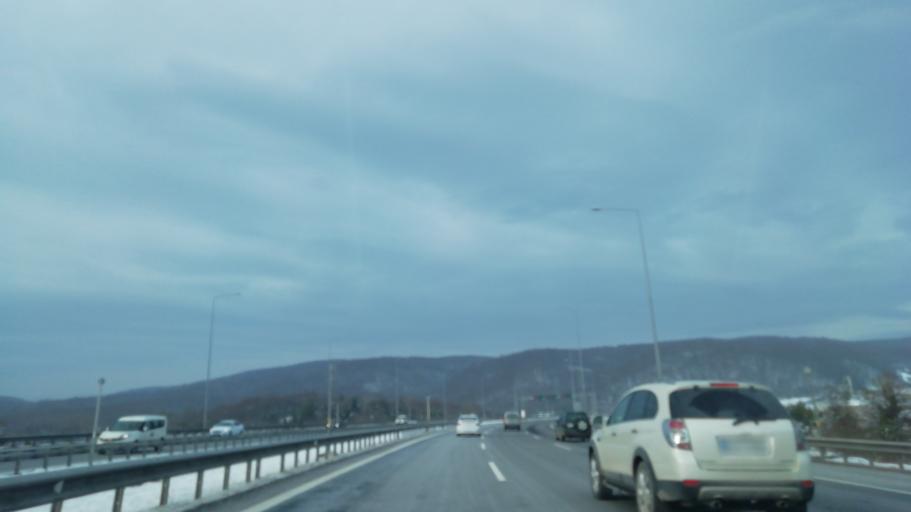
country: TR
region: Duzce
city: Kaynasli
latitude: 40.7288
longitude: 31.4444
